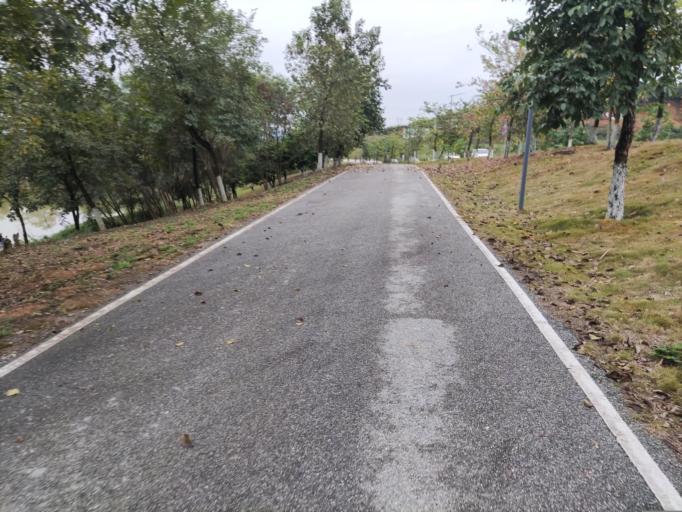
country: CN
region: Guangxi Zhuangzu Zizhiqu
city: Tianzhou
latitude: 23.7808
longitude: 106.7316
